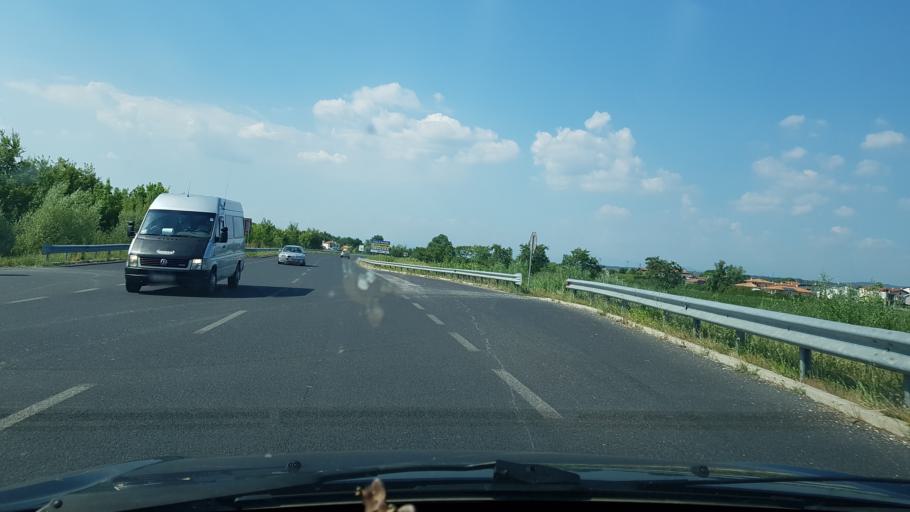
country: IT
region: Friuli Venezia Giulia
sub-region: Provincia di Gorizia
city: Staranzano
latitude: 45.7998
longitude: 13.4890
